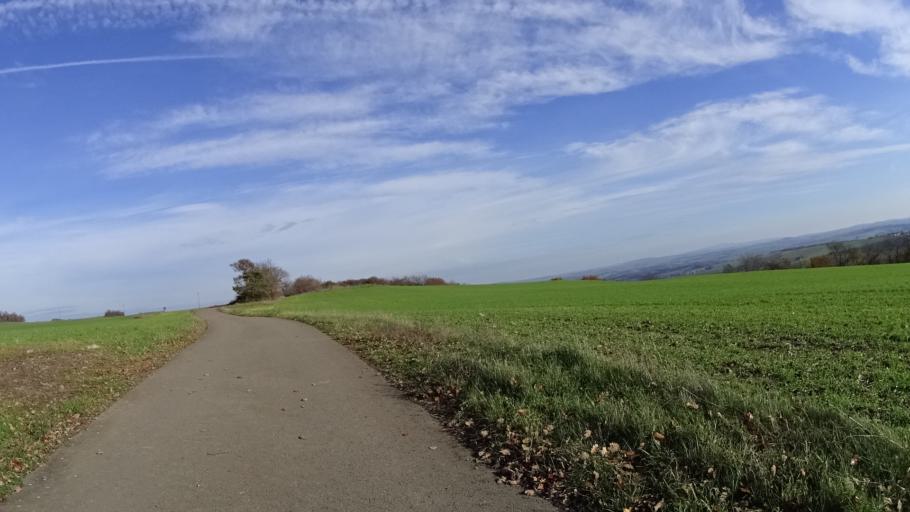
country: DE
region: Rheinland-Pfalz
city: Kirrweiler
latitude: 49.6361
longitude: 7.4923
